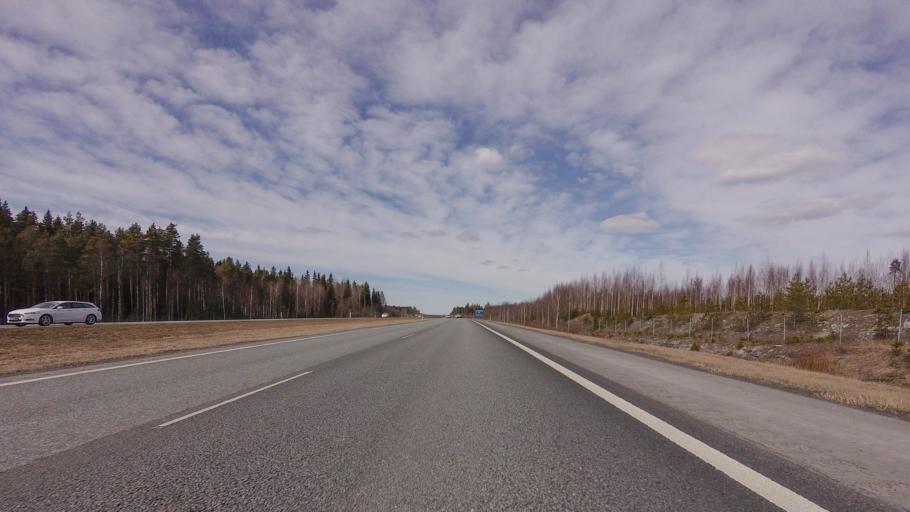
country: FI
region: Pirkanmaa
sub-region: Tampere
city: Lempaeaelae
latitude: 61.3204
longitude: 23.8142
